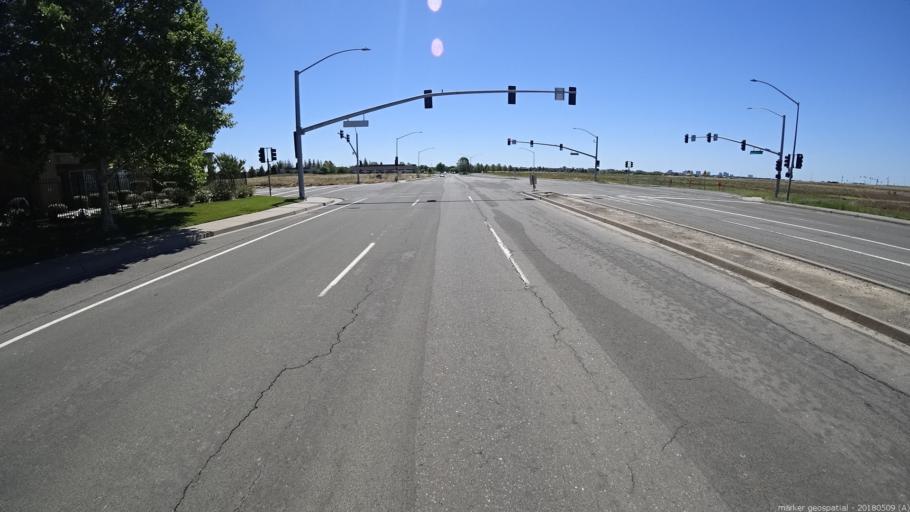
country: US
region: California
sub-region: Yolo County
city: West Sacramento
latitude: 38.6478
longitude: -121.5237
